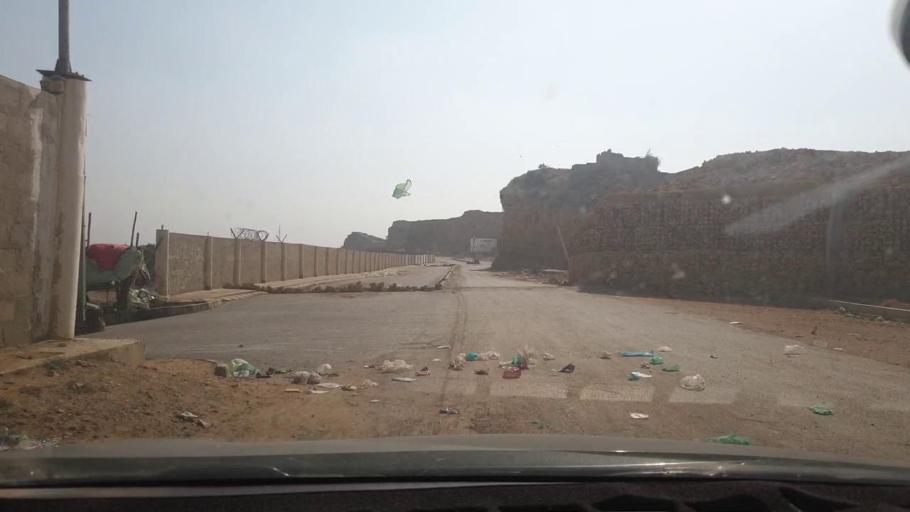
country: PK
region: Sindh
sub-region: Karachi District
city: Karachi
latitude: 24.9696
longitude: 66.9979
